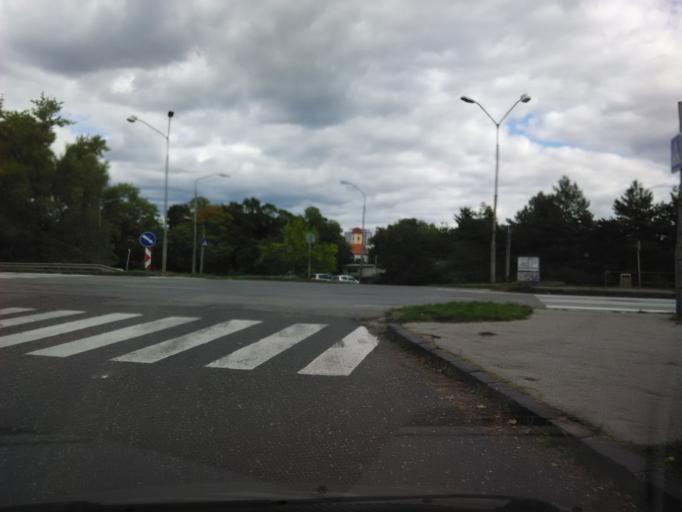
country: SK
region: Nitriansky
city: Levice
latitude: 48.2198
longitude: 18.5986
